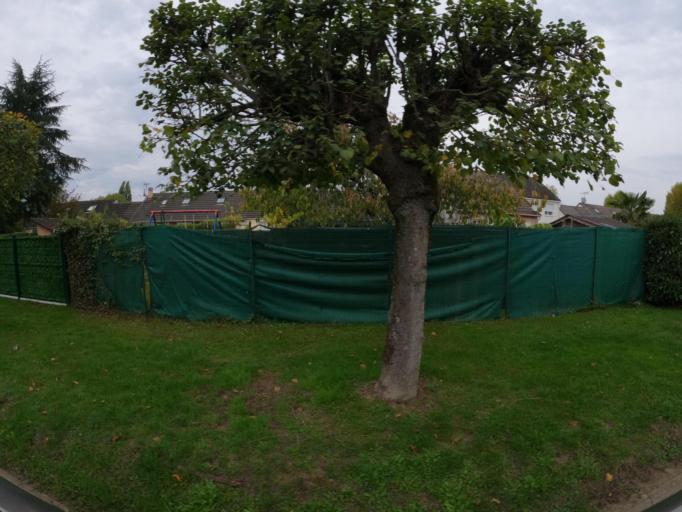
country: FR
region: Ile-de-France
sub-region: Departement de Seine-et-Marne
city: Villeneuve-le-Comte
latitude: 48.8152
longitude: 2.8265
